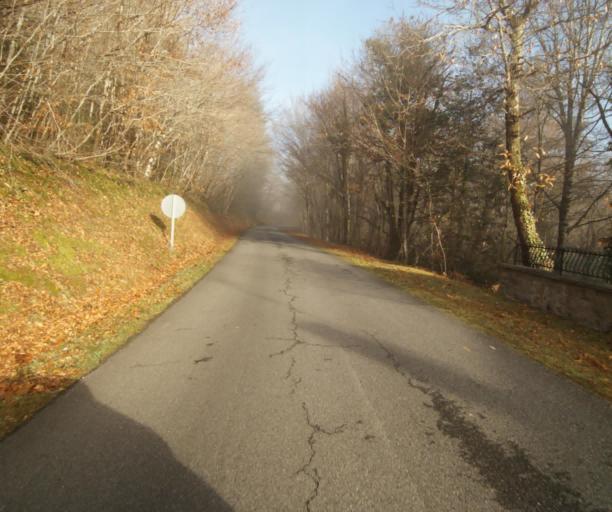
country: FR
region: Limousin
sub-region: Departement de la Correze
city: Laguenne
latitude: 45.2523
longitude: 1.7840
